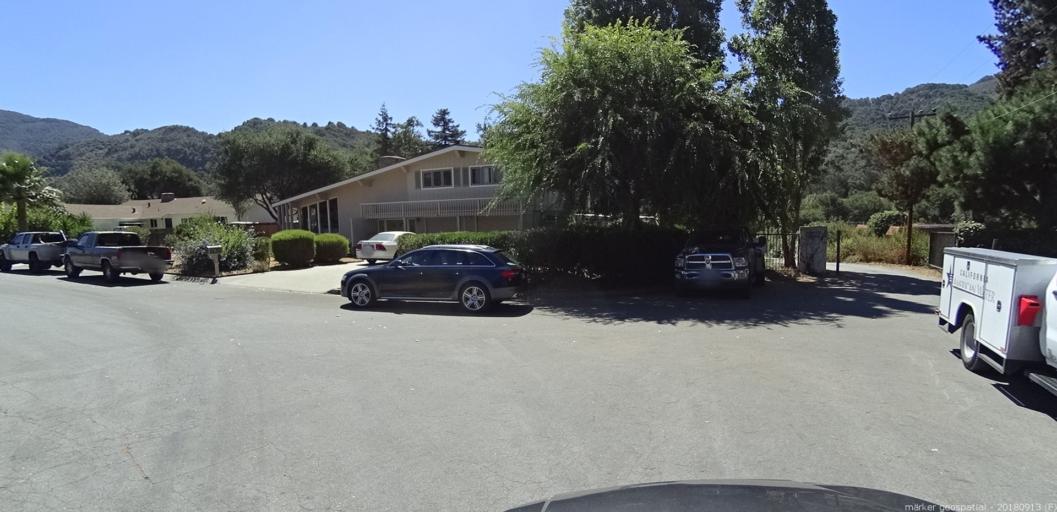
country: US
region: California
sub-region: Monterey County
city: Carmel Valley Village
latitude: 36.5208
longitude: -121.8113
